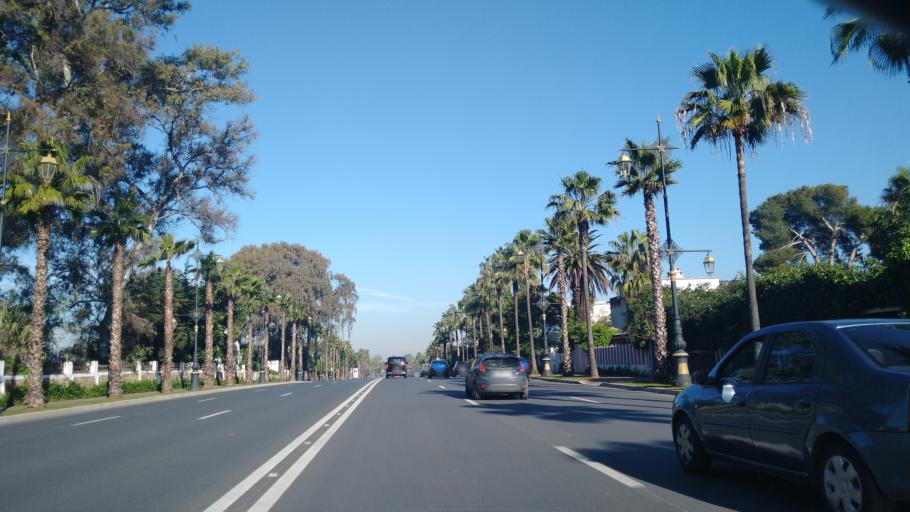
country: MA
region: Rabat-Sale-Zemmour-Zaer
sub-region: Rabat
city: Rabat
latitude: 33.9960
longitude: -6.8274
